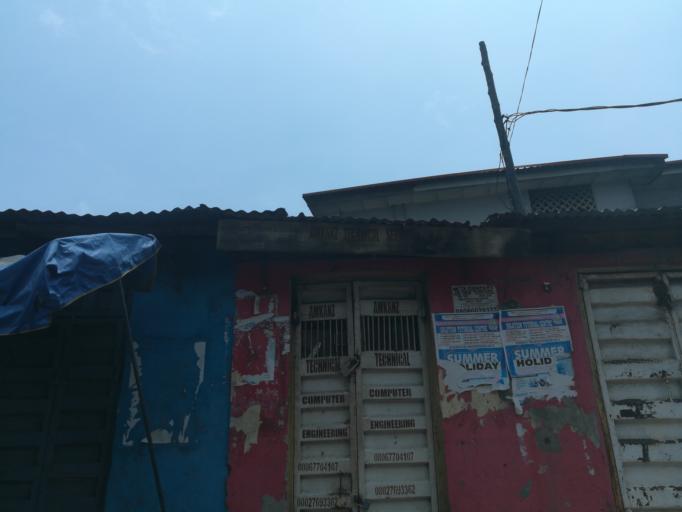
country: NG
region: Lagos
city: Lagos
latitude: 6.4570
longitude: 3.3978
